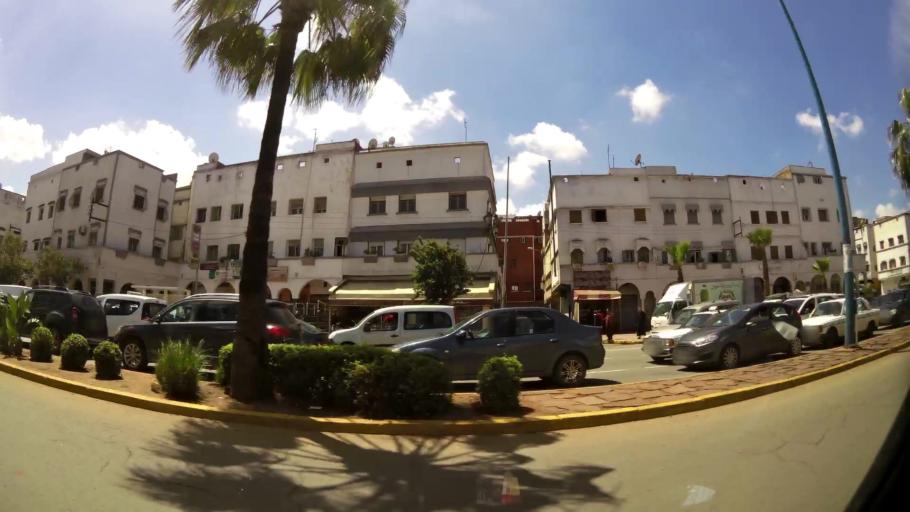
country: MA
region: Grand Casablanca
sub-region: Casablanca
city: Casablanca
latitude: 33.5616
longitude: -7.5655
